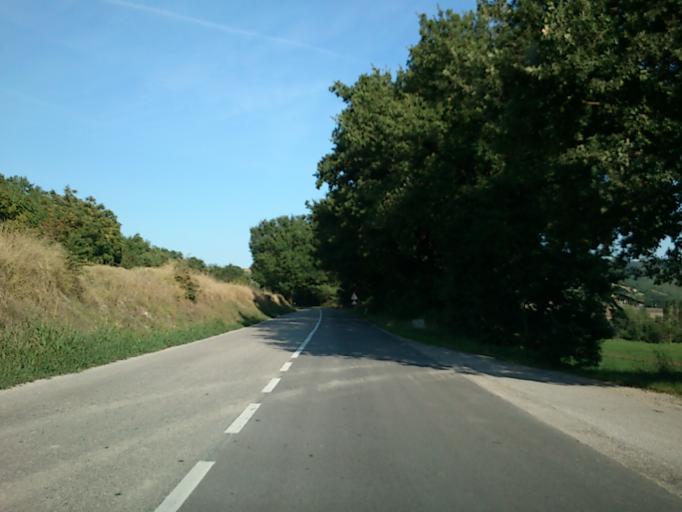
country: IT
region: The Marches
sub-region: Provincia di Pesaro e Urbino
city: Fossombrone
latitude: 43.6770
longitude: 12.7563
